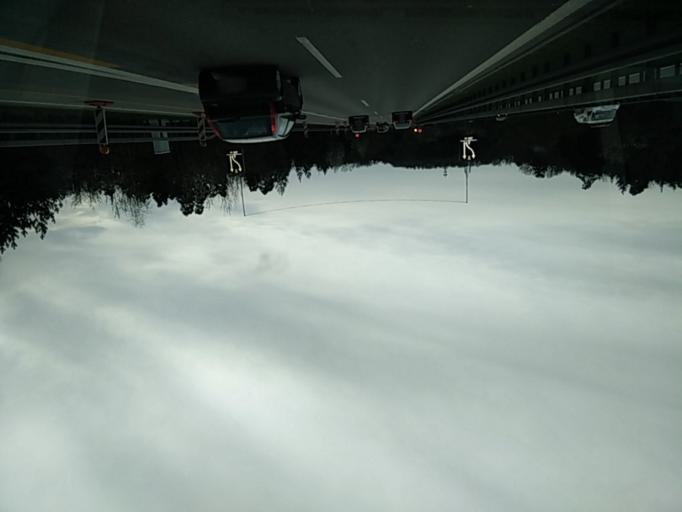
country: DE
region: Baden-Wuerttemberg
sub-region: Regierungsbezirk Stuttgart
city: Nufringen
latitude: 48.6126
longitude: 8.9021
